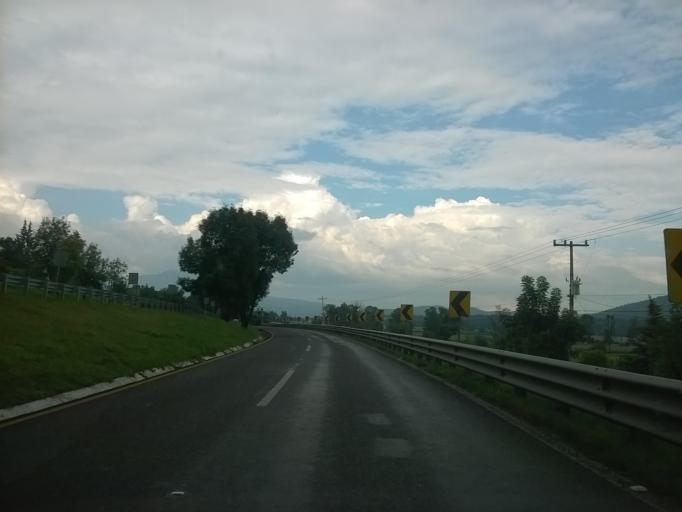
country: MX
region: Michoacan
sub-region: Huiramba
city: El Pedregal
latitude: 19.5314
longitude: -101.4769
